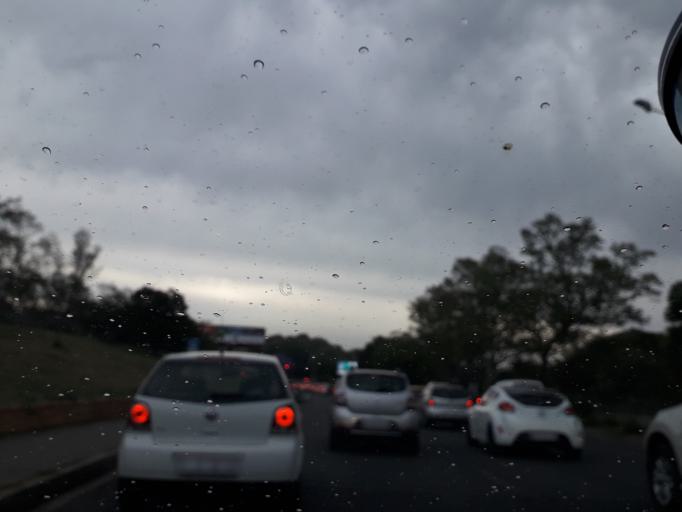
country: ZA
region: Gauteng
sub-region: City of Johannesburg Metropolitan Municipality
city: Johannesburg
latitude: -26.1004
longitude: 28.0351
